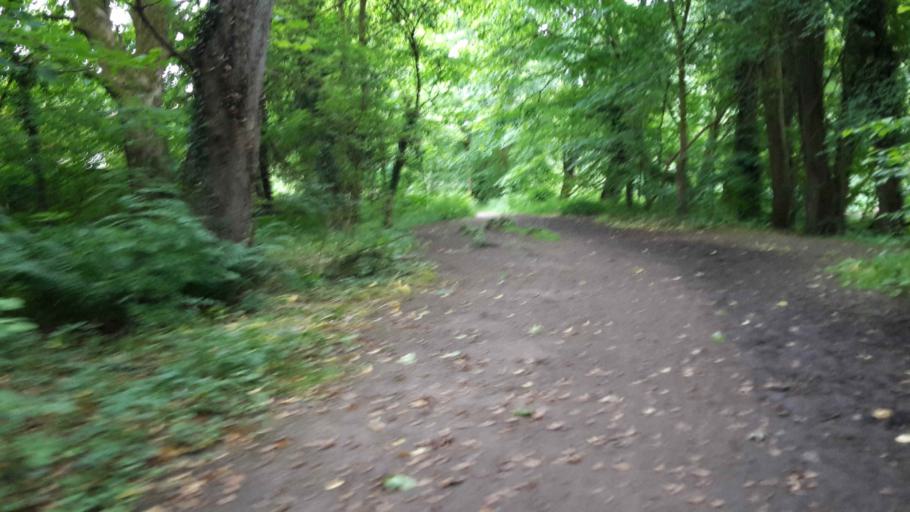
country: GB
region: Scotland
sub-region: South Lanarkshire
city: Uddingston
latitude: 55.8038
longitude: -4.0933
